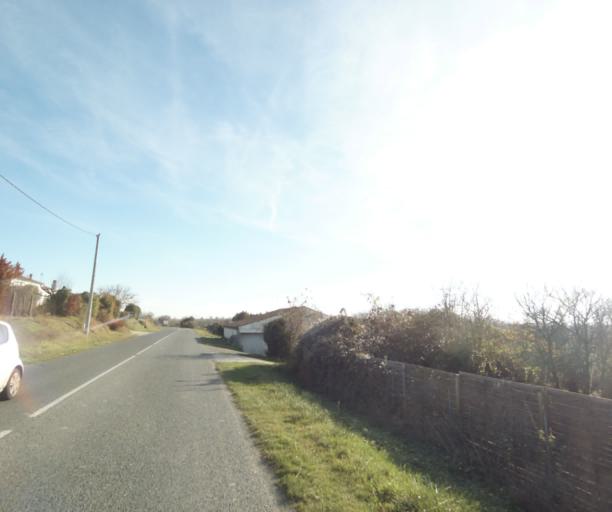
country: FR
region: Poitou-Charentes
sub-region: Departement de la Charente-Maritime
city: Chaniers
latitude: 45.7241
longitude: -0.5715
